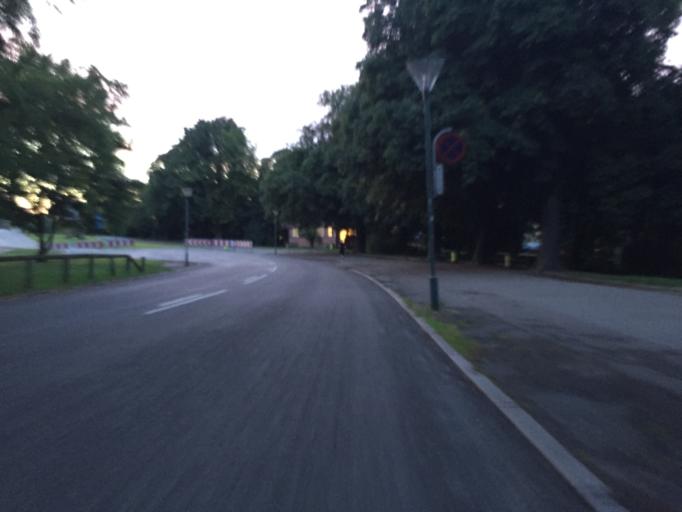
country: DK
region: Capital Region
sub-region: Kobenhavn
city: Christianshavn
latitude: 55.6939
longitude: 12.5952
